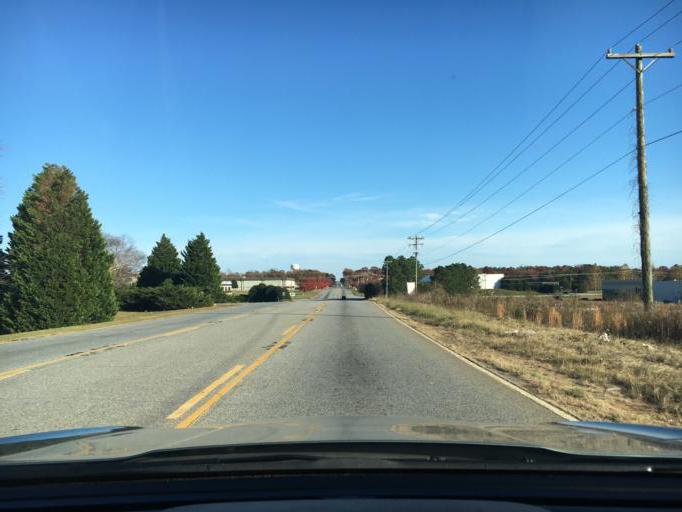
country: US
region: South Carolina
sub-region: Spartanburg County
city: Southern Shops
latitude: 34.9935
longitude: -82.0384
